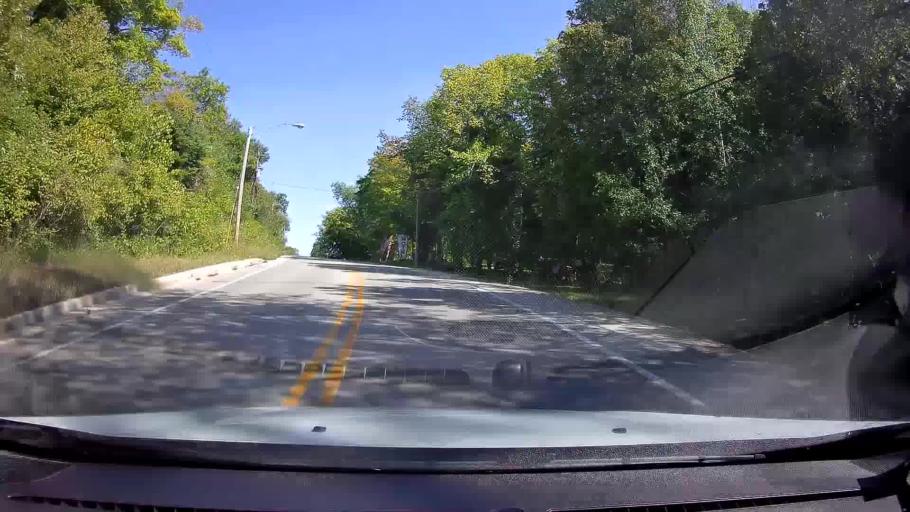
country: US
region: Michigan
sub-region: Delta County
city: Escanaba
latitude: 45.2892
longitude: -87.0165
